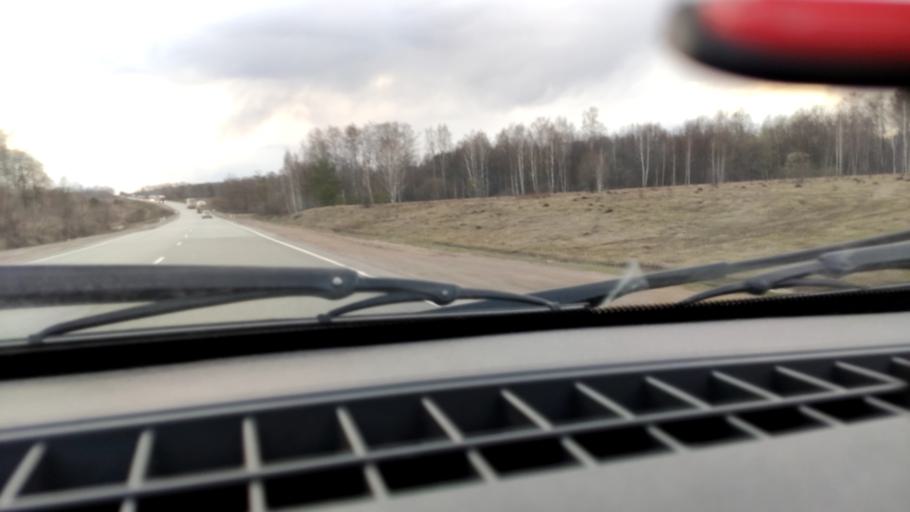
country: RU
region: Bashkortostan
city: Kudeyevskiy
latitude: 54.8165
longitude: 56.7082
